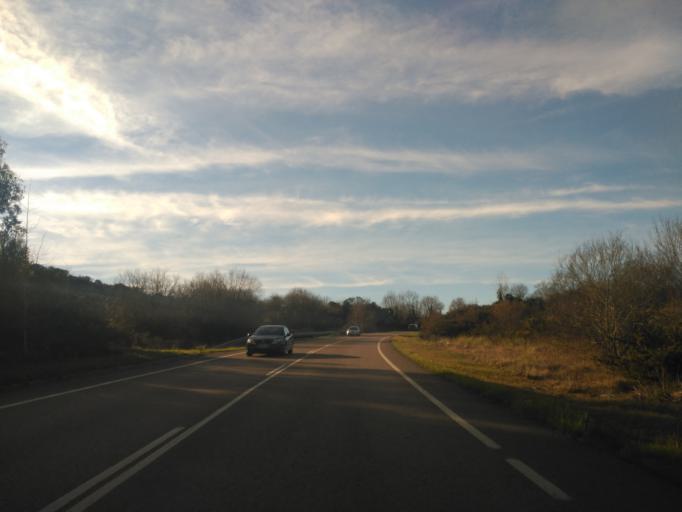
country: ES
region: Cantabria
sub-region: Provincia de Cantabria
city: Comillas
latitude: 43.3574
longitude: -4.2655
